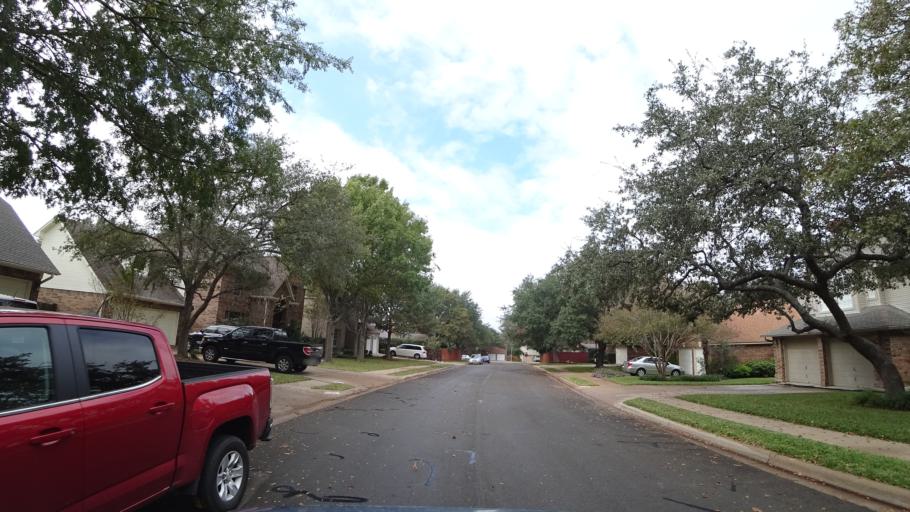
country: US
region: Texas
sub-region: Williamson County
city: Brushy Creek
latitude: 30.5178
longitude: -97.7142
